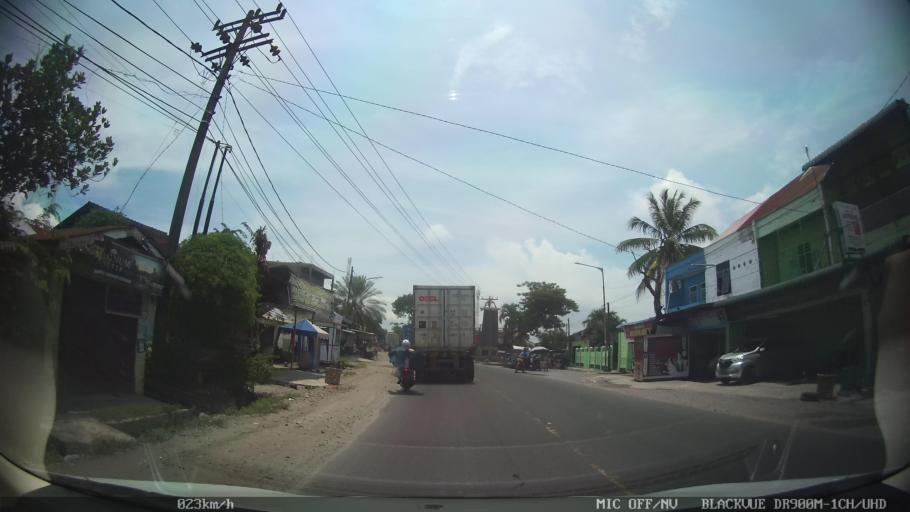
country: ID
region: North Sumatra
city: Labuhan Deli
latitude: 3.7400
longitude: 98.6753
